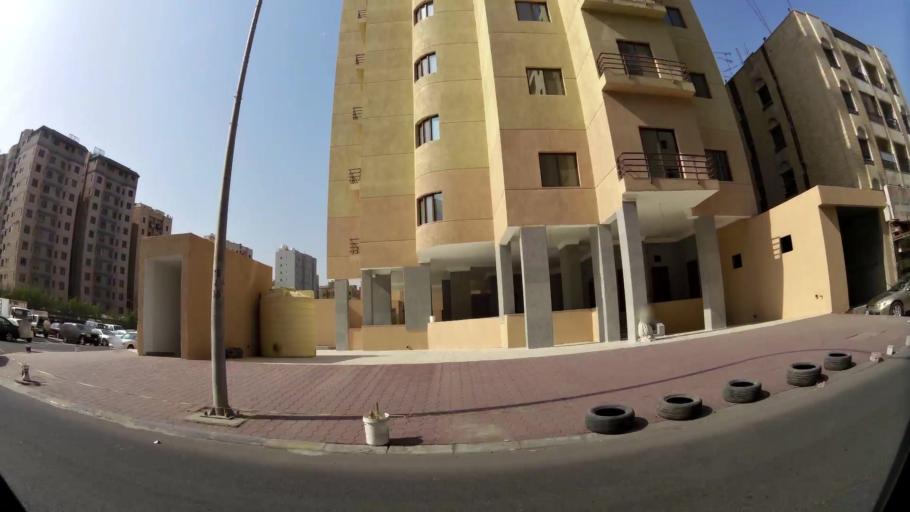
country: KW
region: Muhafazat Hawalli
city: Hawalli
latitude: 29.3282
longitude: 48.0177
